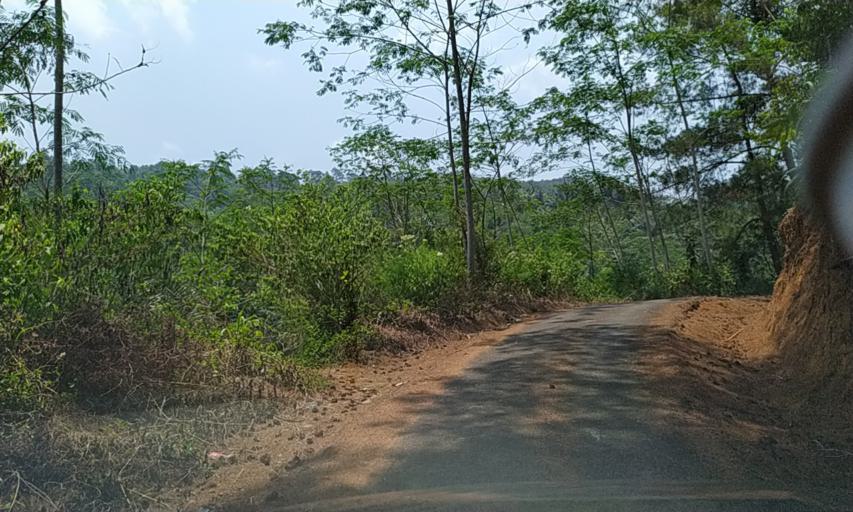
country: ID
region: Central Java
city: Kaduluhur
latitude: -7.1913
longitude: 108.6526
